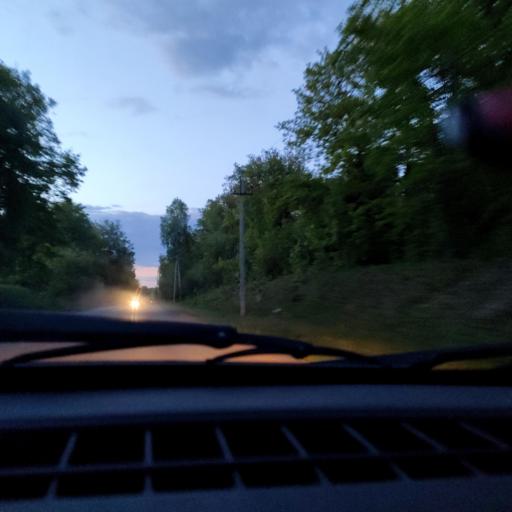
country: RU
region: Bashkortostan
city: Avdon
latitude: 54.6509
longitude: 55.5812
